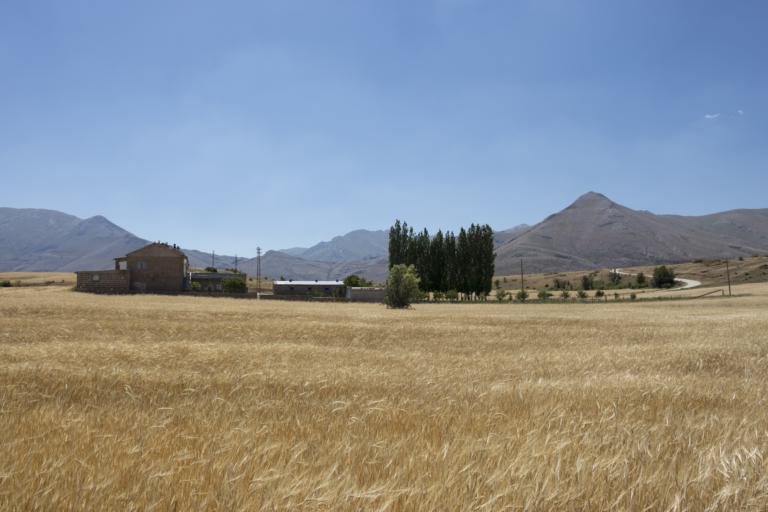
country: TR
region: Kayseri
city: Toklar
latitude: 38.4106
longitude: 36.0846
